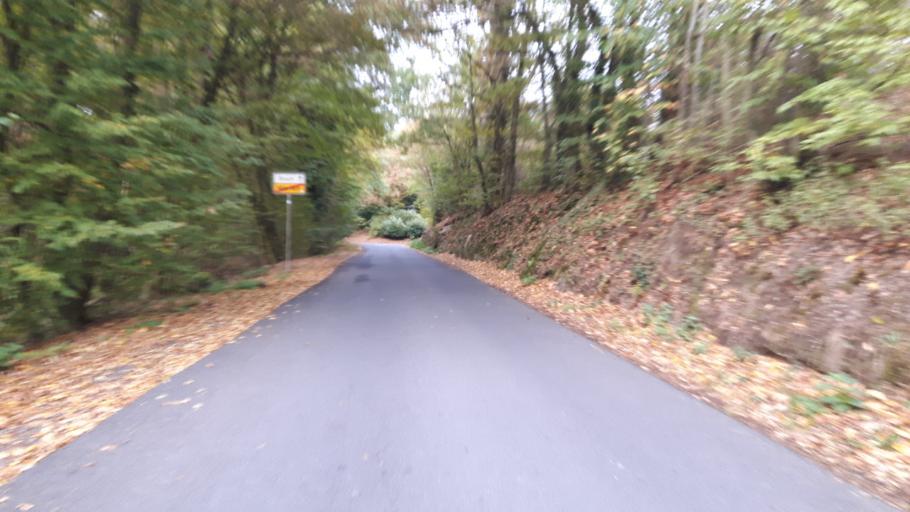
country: DE
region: North Rhine-Westphalia
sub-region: Regierungsbezirk Koln
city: Eitorf
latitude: 50.7703
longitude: 7.3958
